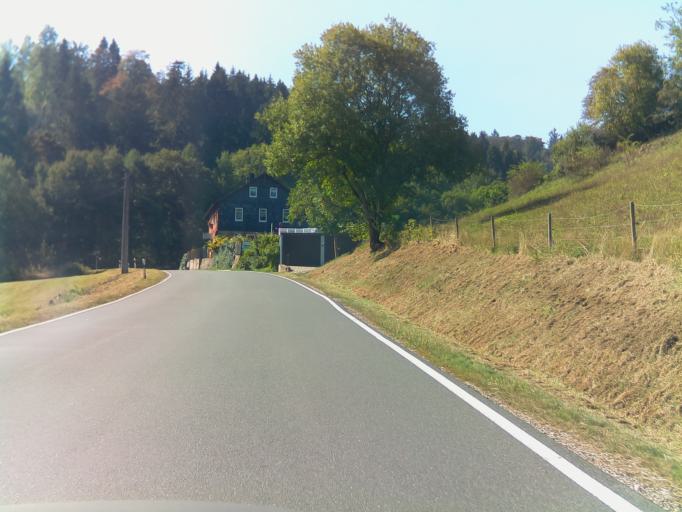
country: DE
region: Thuringia
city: Wurzbach
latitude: 50.4899
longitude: 11.4836
